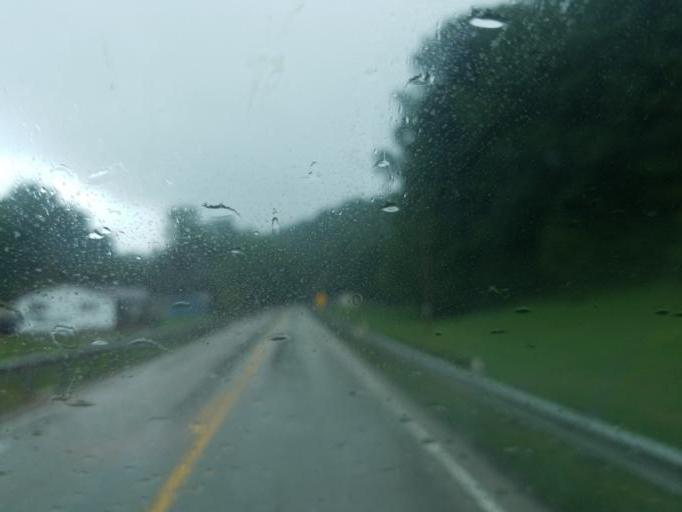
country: US
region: Kentucky
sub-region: Rowan County
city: Morehead
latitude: 38.2560
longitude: -83.3351
